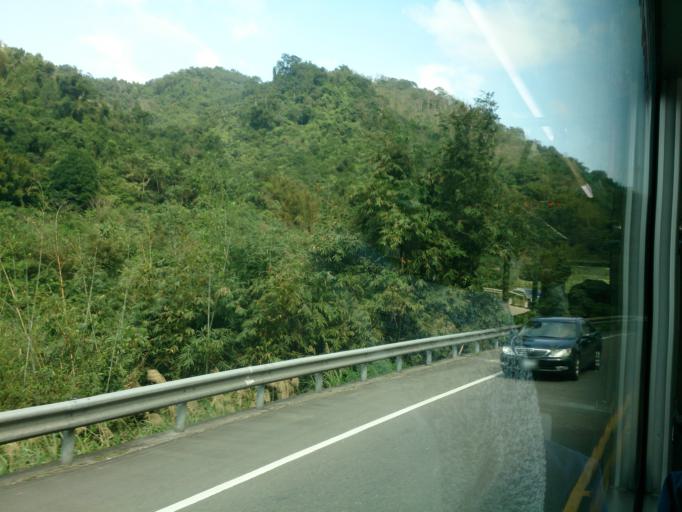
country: TW
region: Taipei
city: Taipei
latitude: 25.0075
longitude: 121.6545
